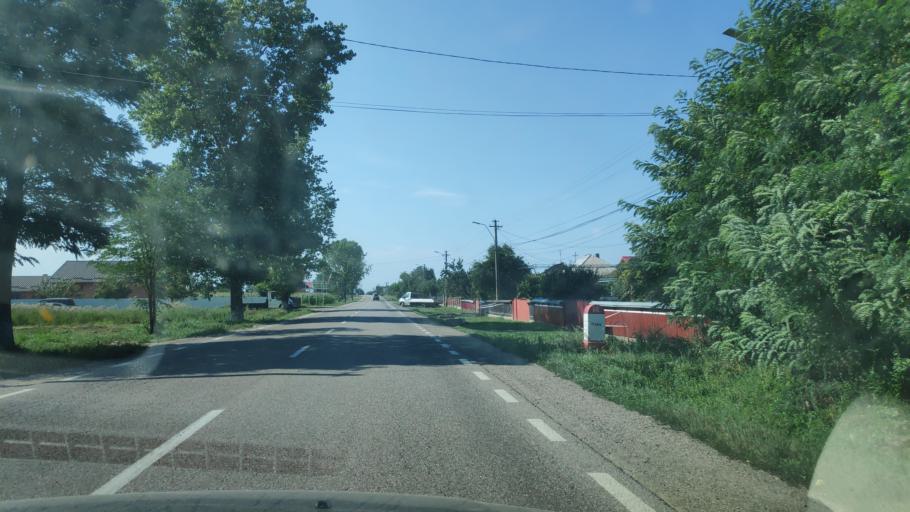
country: RO
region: Suceava
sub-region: Comuna Boroaia
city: Boroaia
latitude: 47.3765
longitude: 26.3222
